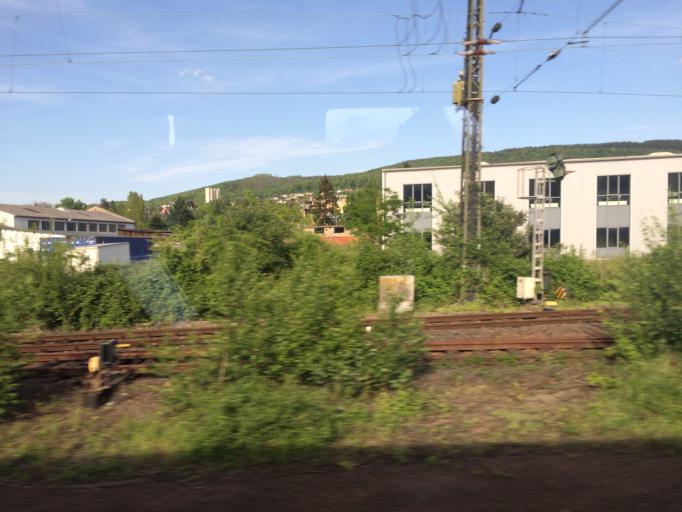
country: DE
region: Rheinland-Pfalz
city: Lahnstein
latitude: 50.3224
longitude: 7.5947
